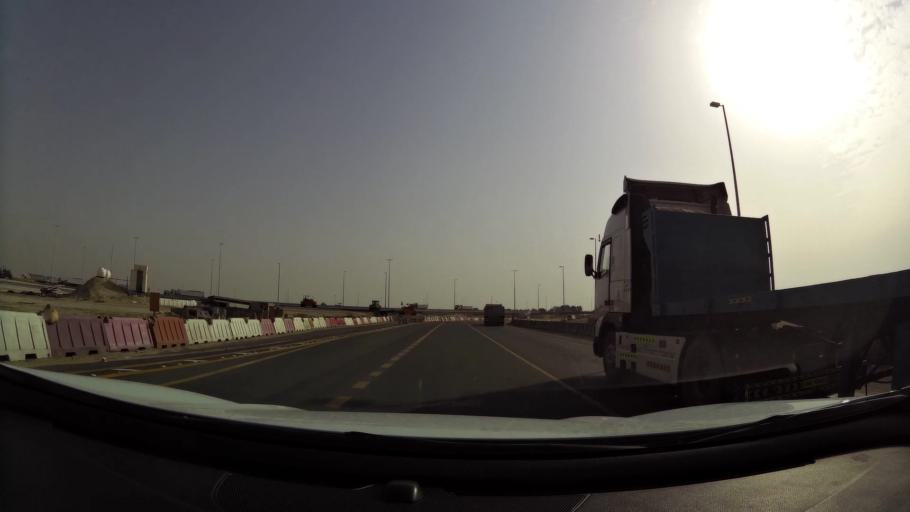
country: AE
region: Abu Dhabi
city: Abu Dhabi
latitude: 24.2869
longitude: 54.5451
